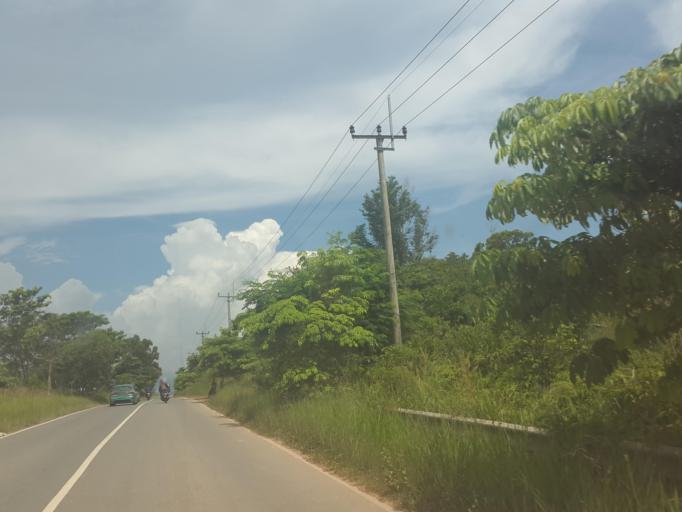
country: ID
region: Riau Islands
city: Tanjungpinang
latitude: 0.9300
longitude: 104.1129
